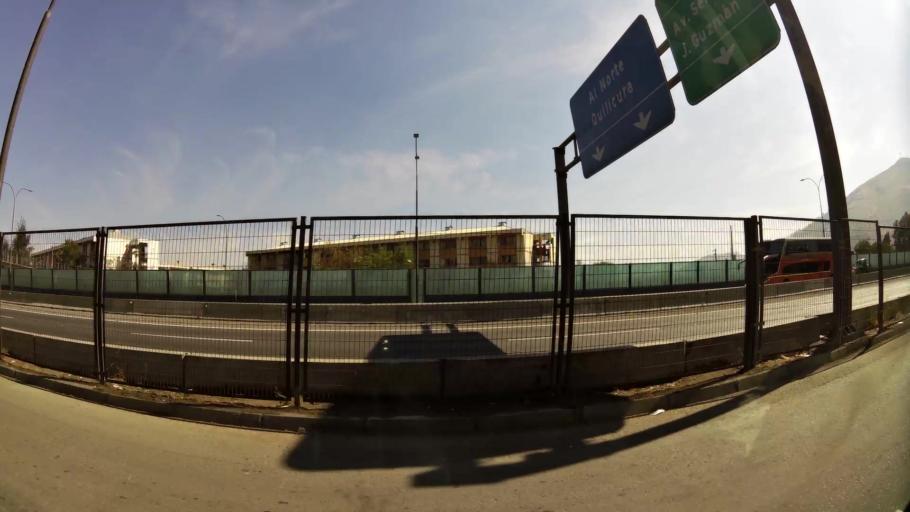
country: CL
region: Santiago Metropolitan
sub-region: Provincia de Santiago
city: Lo Prado
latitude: -33.4034
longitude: -70.6959
